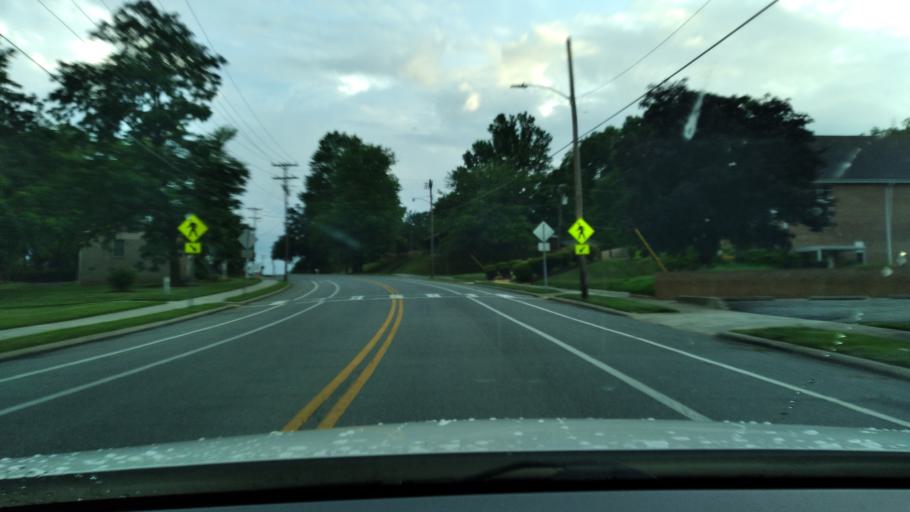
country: US
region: North Carolina
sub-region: Guilford County
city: Greensboro
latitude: 36.0542
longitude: -79.7790
